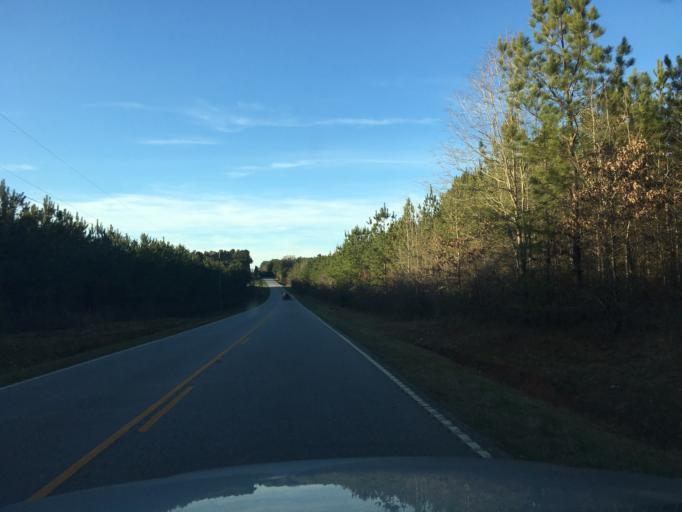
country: US
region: South Carolina
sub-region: Saluda County
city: Saluda
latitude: 34.0727
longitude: -81.8191
